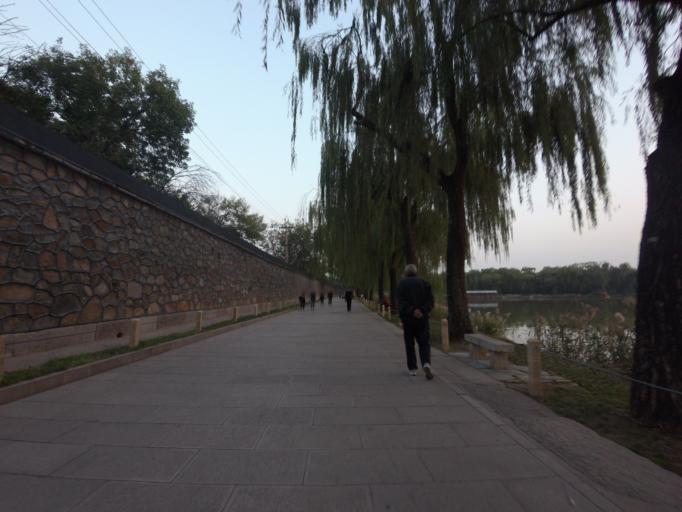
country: CN
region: Beijing
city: Haidian
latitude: 39.9819
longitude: 116.2731
